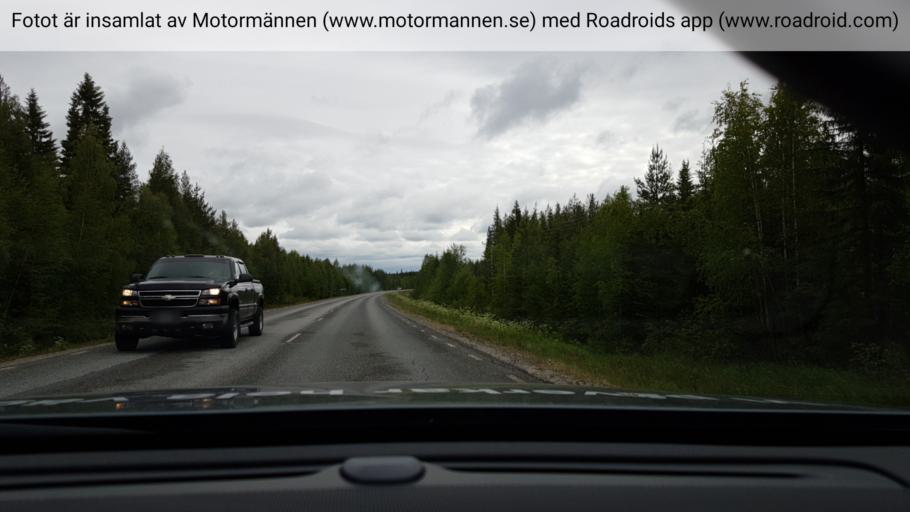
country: SE
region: Vaesterbotten
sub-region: Lycksele Kommun
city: Lycksele
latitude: 64.5612
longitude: 18.5290
